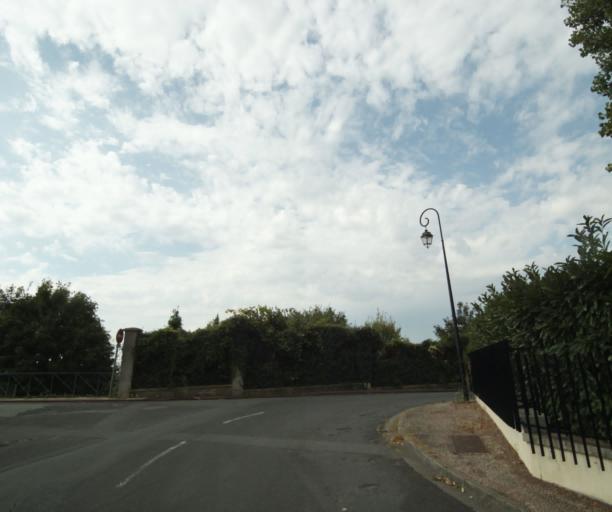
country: FR
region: Poitou-Charentes
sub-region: Departement de la Charente-Maritime
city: Tonnay-Charente
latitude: 45.9417
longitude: -0.8853
